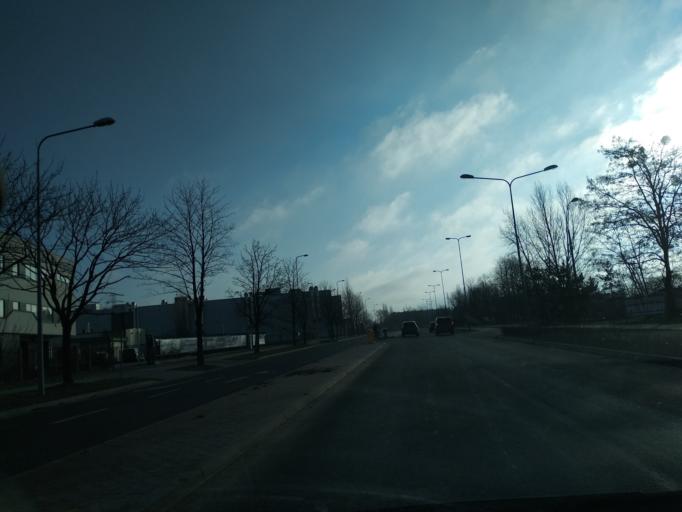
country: PL
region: Masovian Voivodeship
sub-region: Powiat piaseczynski
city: Piaseczno
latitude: 52.0879
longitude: 21.0143
